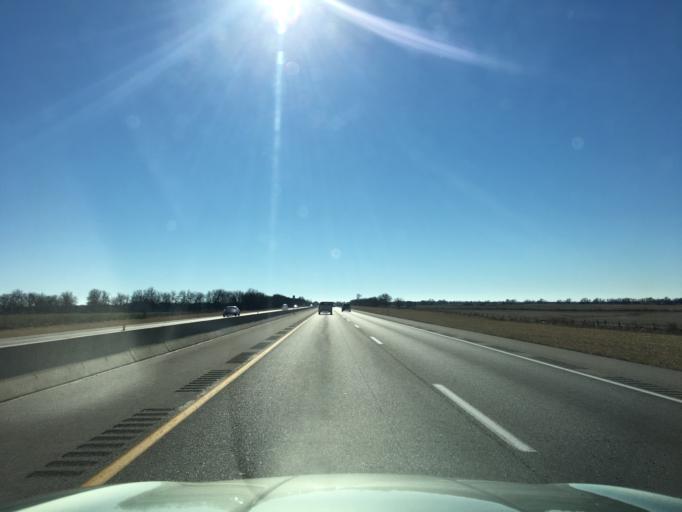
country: US
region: Kansas
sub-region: Sumner County
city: Wellington
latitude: 37.1039
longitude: -97.3387
